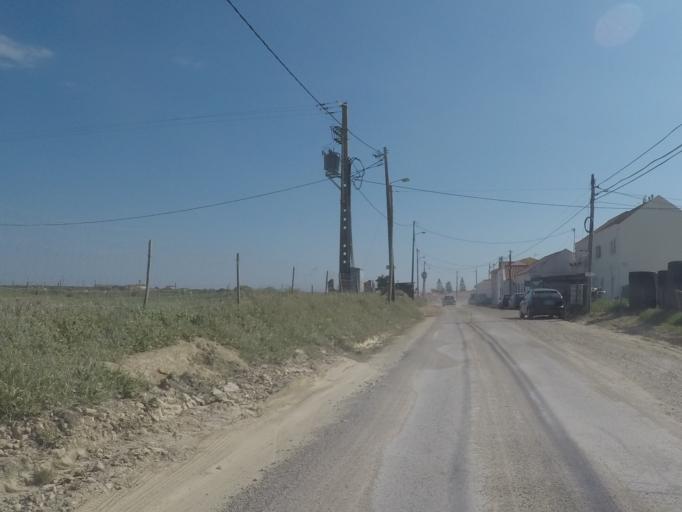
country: PT
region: Setubal
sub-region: Sesimbra
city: Sesimbra
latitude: 38.4326
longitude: -9.1837
